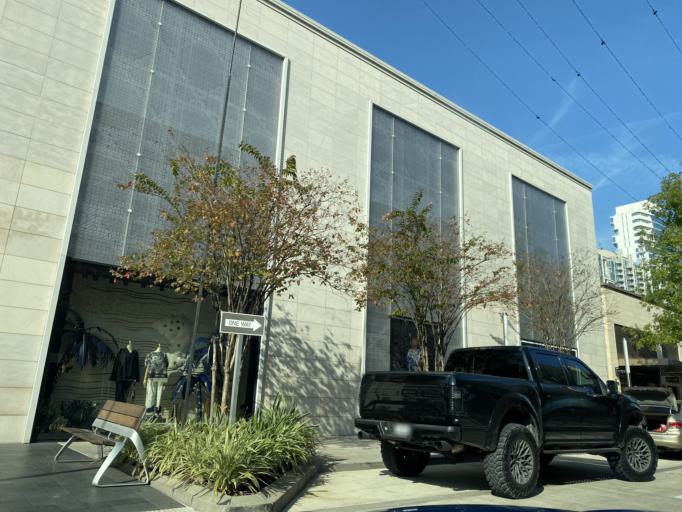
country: US
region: Texas
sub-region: Harris County
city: West University Place
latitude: 29.7429
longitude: -95.4533
